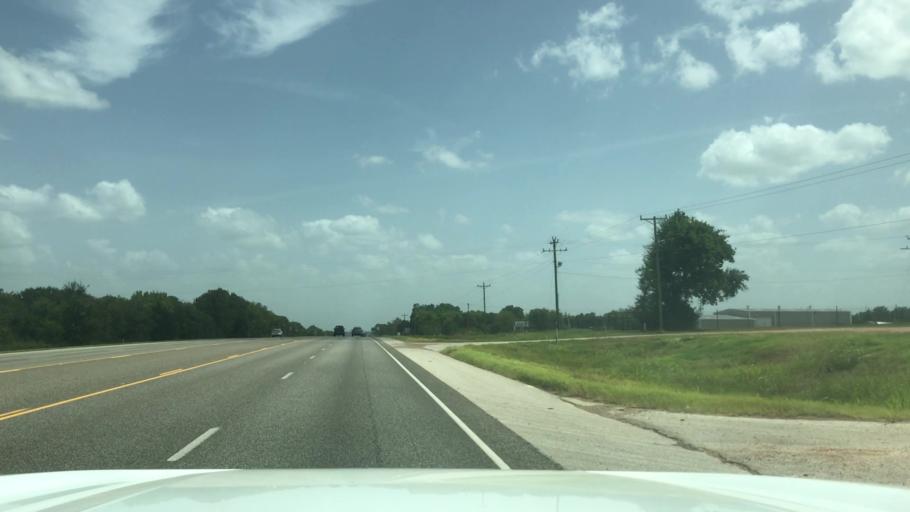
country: US
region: Texas
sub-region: Robertson County
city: Calvert
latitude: 30.9672
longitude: -96.6645
